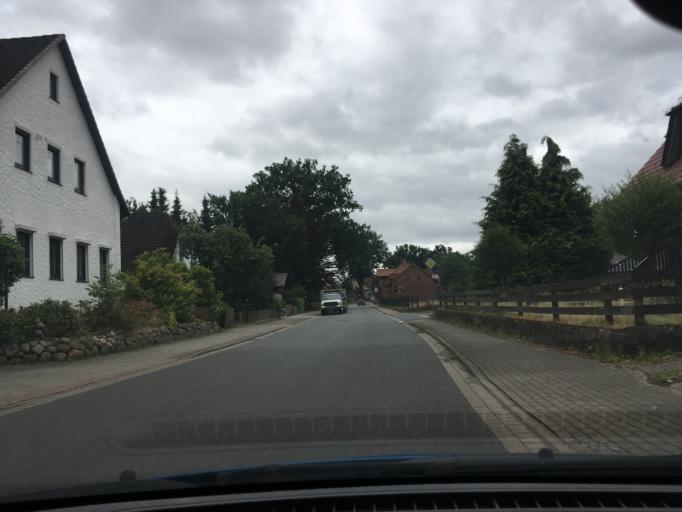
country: DE
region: Lower Saxony
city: Garlstorf
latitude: 53.2396
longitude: 10.1016
